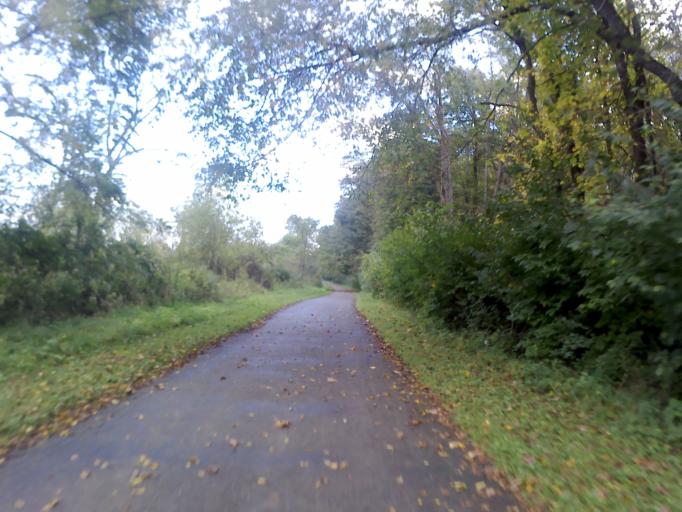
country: US
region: Illinois
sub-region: Will County
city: Bolingbrook
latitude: 41.7104
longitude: -88.0953
